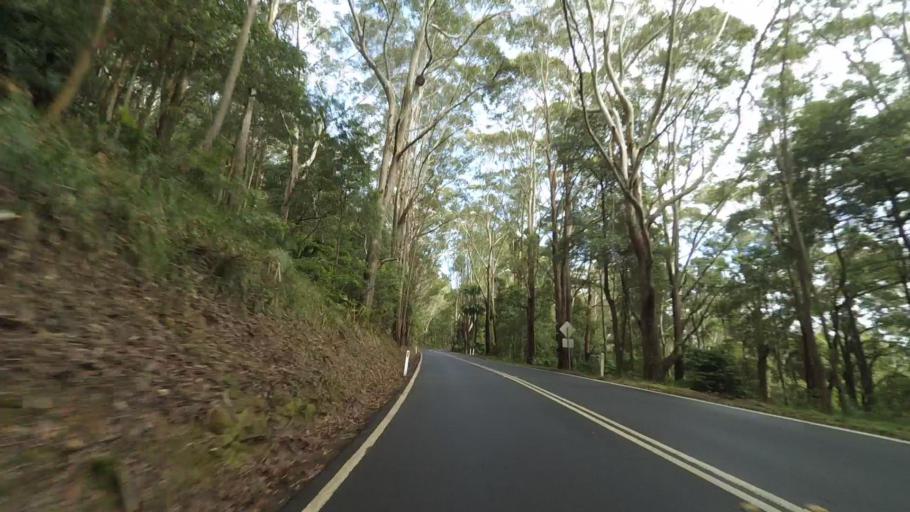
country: AU
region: New South Wales
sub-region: Wollongong
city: Helensburgh
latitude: -34.2045
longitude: 151.0103
